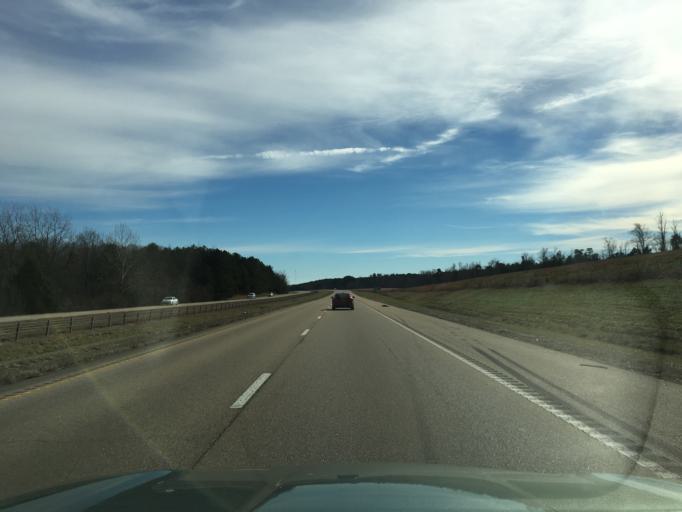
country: US
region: Mississippi
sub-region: Union County
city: New Albany
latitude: 34.3791
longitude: -88.8812
